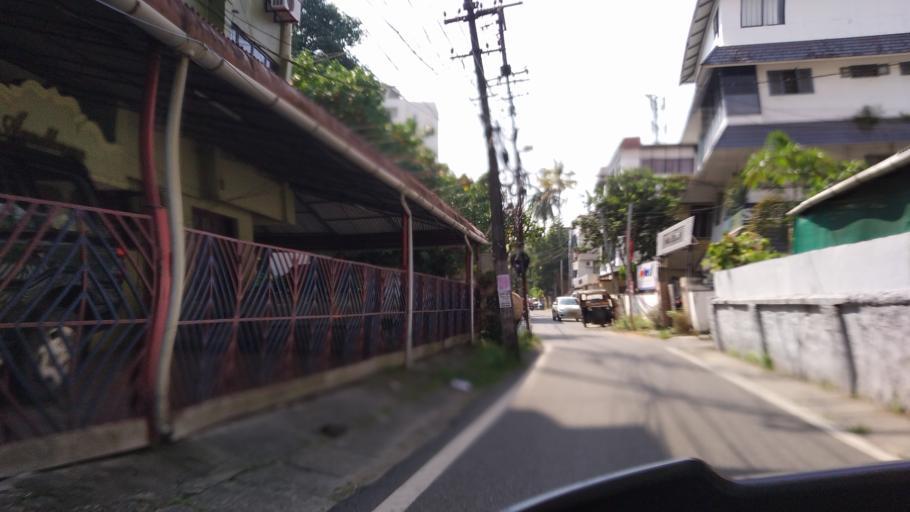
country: IN
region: Kerala
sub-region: Ernakulam
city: Cochin
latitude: 9.9739
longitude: 76.2885
